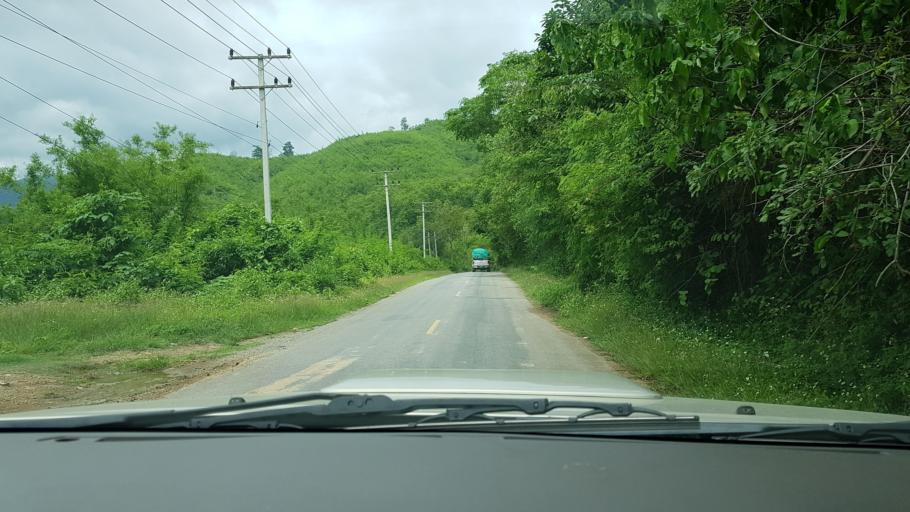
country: TH
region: Nan
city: Chaloem Phra Kiat
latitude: 19.9603
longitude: 101.2584
